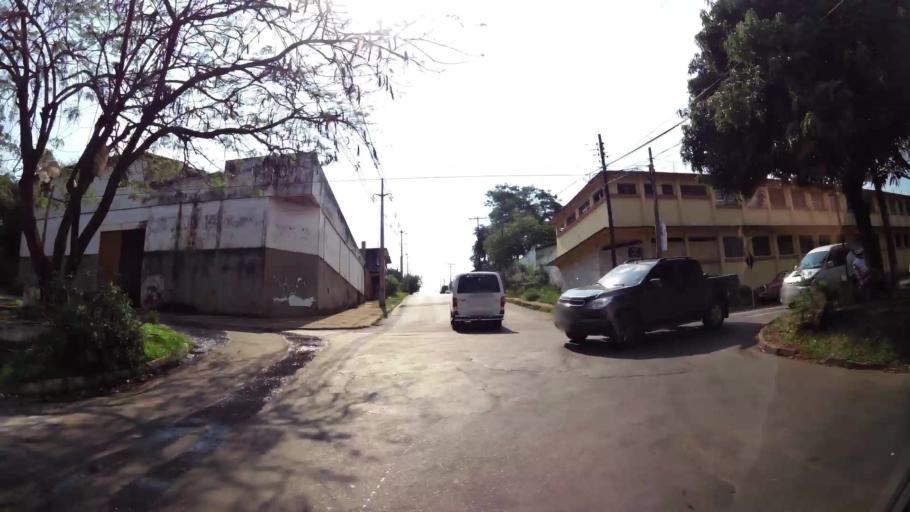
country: PY
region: Alto Parana
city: Ciudad del Este
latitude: -25.5043
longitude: -54.6287
